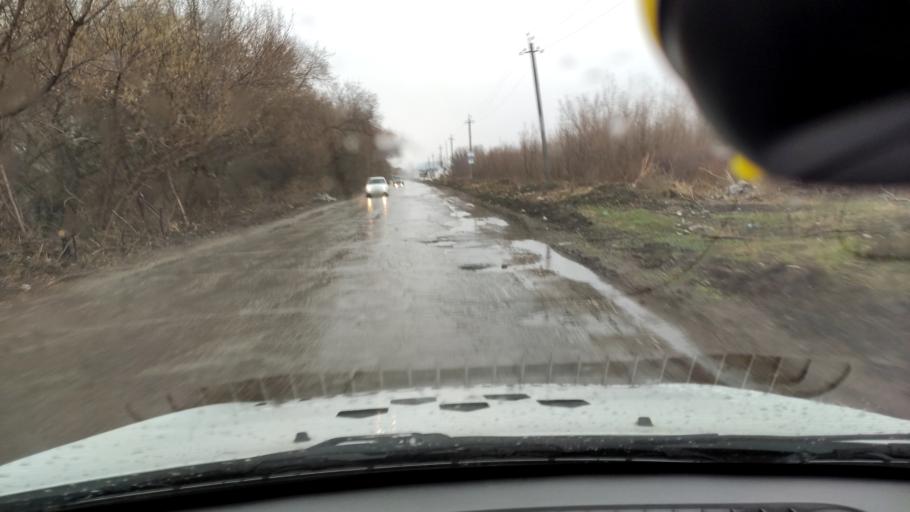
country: RU
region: Samara
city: Podstepki
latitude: 53.5869
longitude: 49.2216
